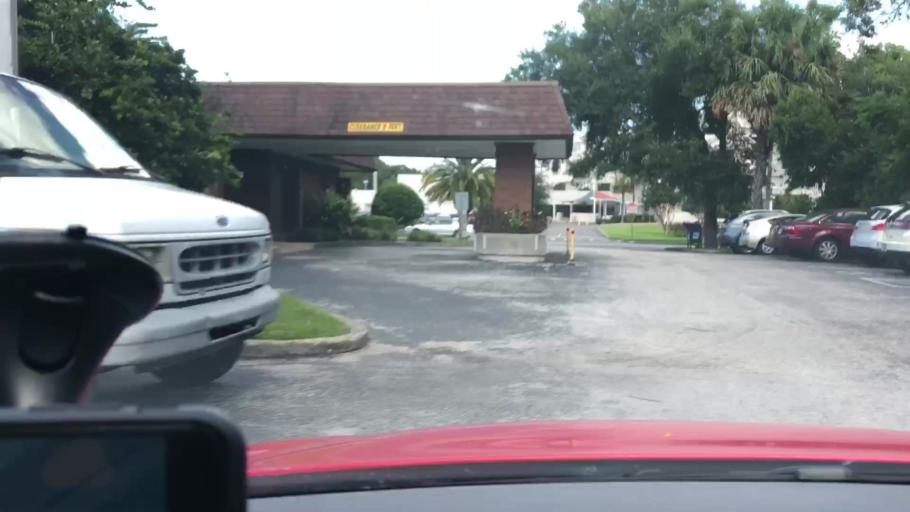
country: US
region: Florida
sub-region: Volusia County
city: DeLand
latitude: 29.0421
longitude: -81.3174
